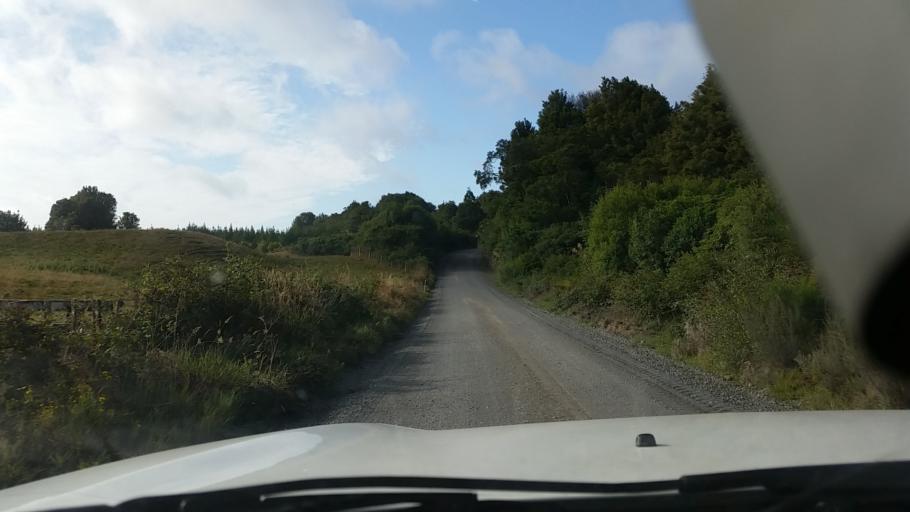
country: NZ
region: Bay of Plenty
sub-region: Rotorua District
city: Rotorua
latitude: -38.1644
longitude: 176.0889
